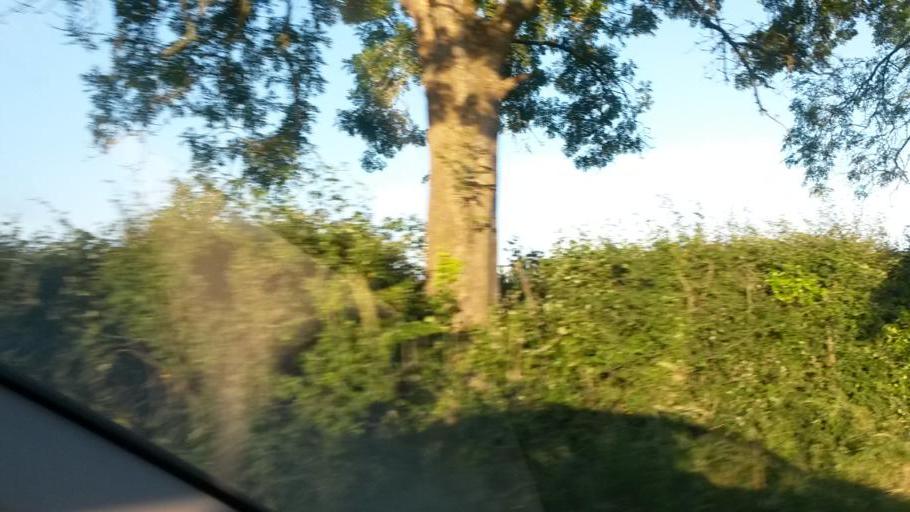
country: IE
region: Leinster
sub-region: An Mhi
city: Ashbourne
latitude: 53.4821
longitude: -6.3169
